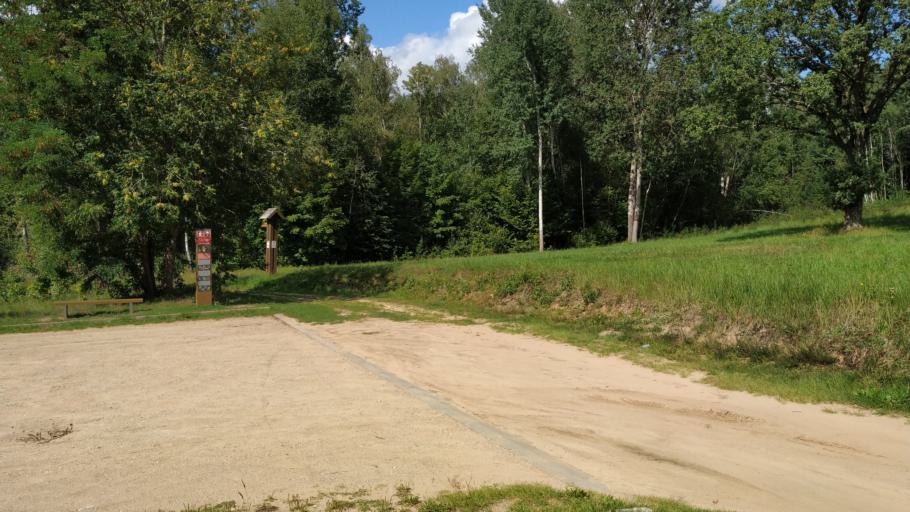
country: LT
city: Grigiskes
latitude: 54.8054
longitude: 24.9849
